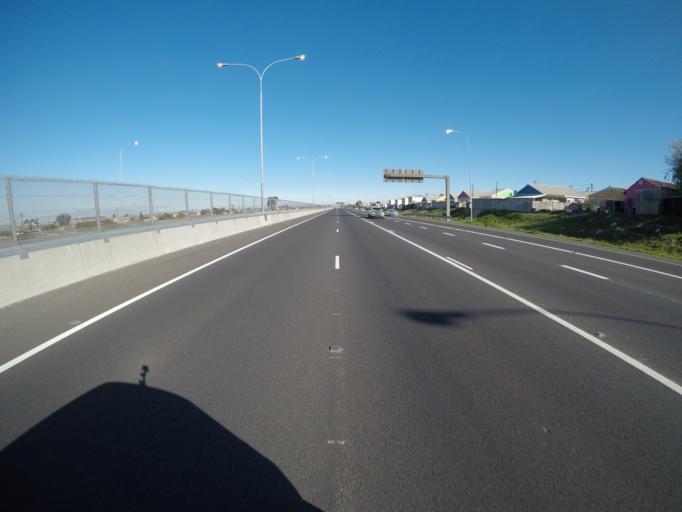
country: ZA
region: Western Cape
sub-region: City of Cape Town
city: Kraaifontein
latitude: -33.9597
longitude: 18.6563
